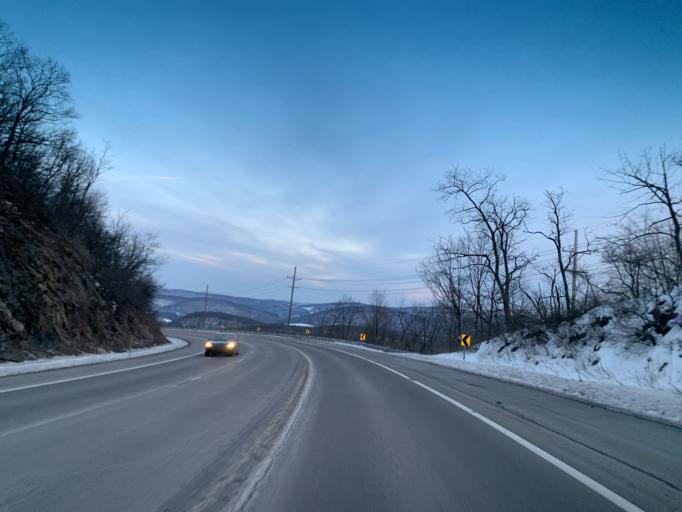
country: US
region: Maryland
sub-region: Allegany County
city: Cumberland
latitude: 39.7034
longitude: -78.6197
